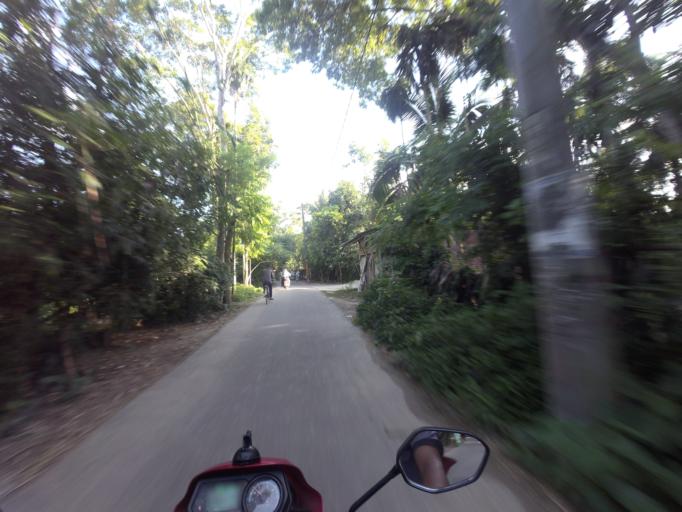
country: BD
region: Khulna
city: Bhatpara Abhaynagar
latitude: 22.9219
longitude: 89.5175
